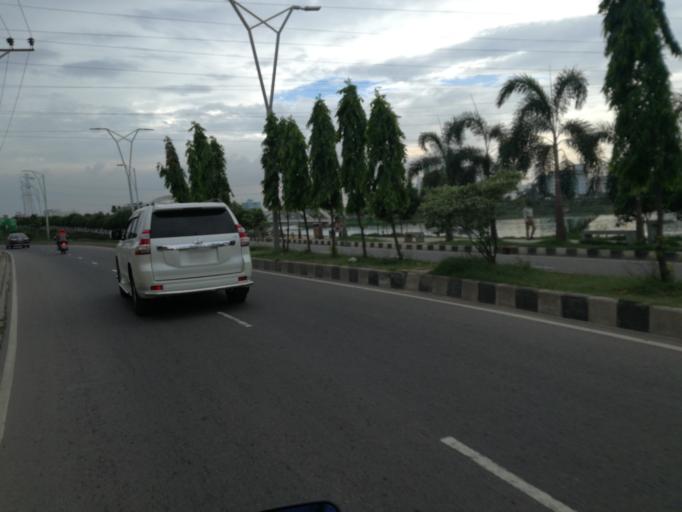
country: BD
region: Dhaka
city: Paltan
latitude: 23.7685
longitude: 90.4161
